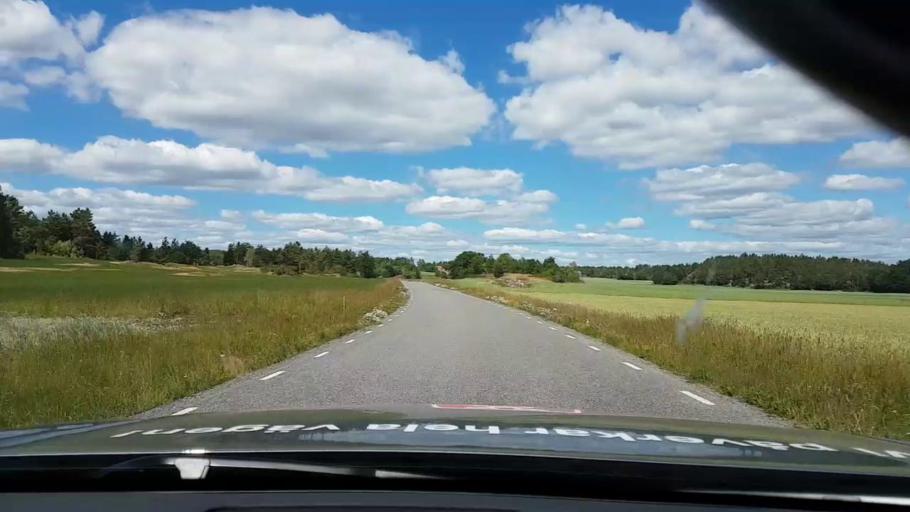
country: SE
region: Kalmar
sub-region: Vasterviks Kommun
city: Forserum
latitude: 58.0027
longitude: 16.5895
